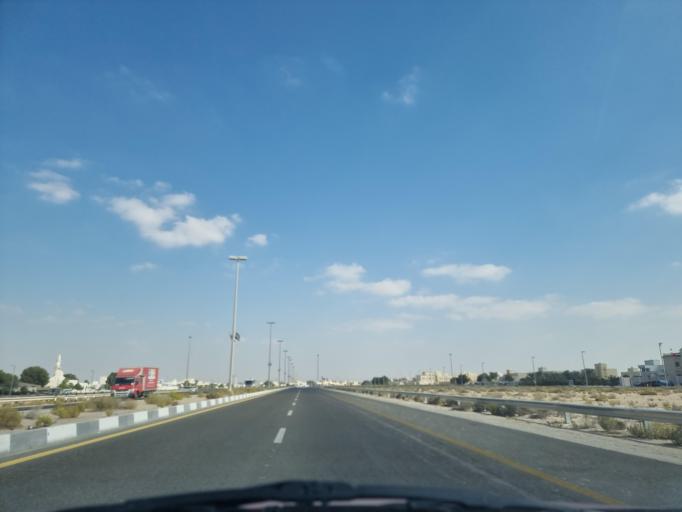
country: AE
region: Abu Dhabi
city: Abu Dhabi
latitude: 24.4032
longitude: 54.7364
